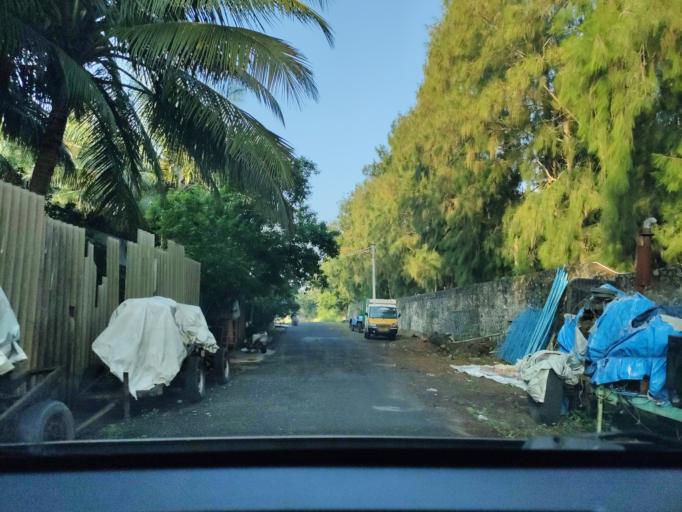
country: IN
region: Tamil Nadu
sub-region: Villupuram
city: Auroville
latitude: 12.0647
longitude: 79.8813
